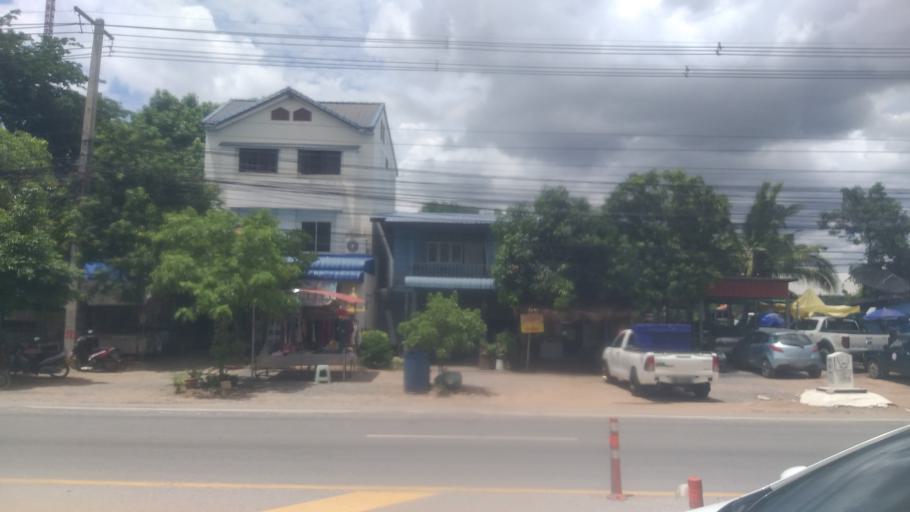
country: TH
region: Nakhon Ratchasima
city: Nakhon Ratchasima
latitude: 15.0790
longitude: 102.1154
